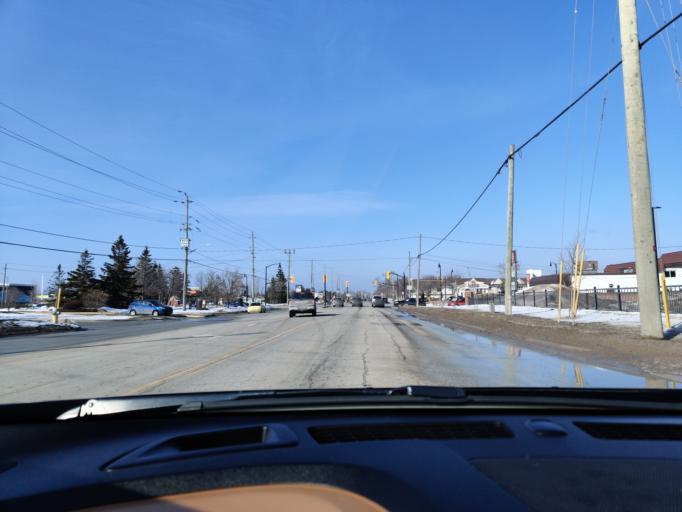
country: CA
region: Ontario
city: Collingwood
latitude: 44.5001
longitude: -80.2342
